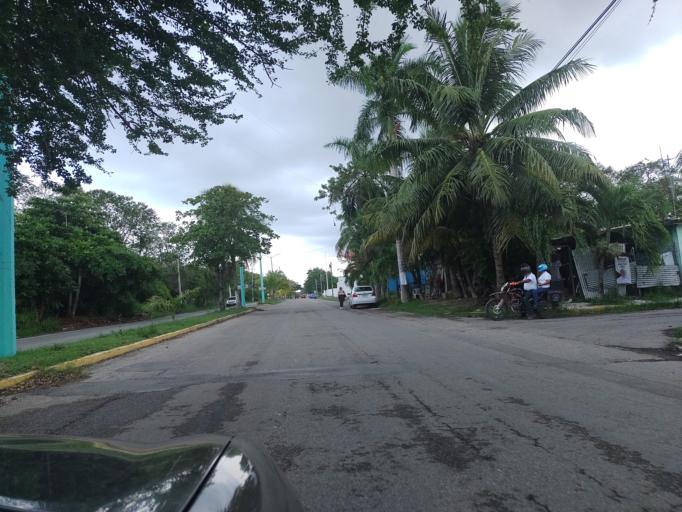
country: MX
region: Quintana Roo
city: Chetumal
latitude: 18.5162
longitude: -88.2782
